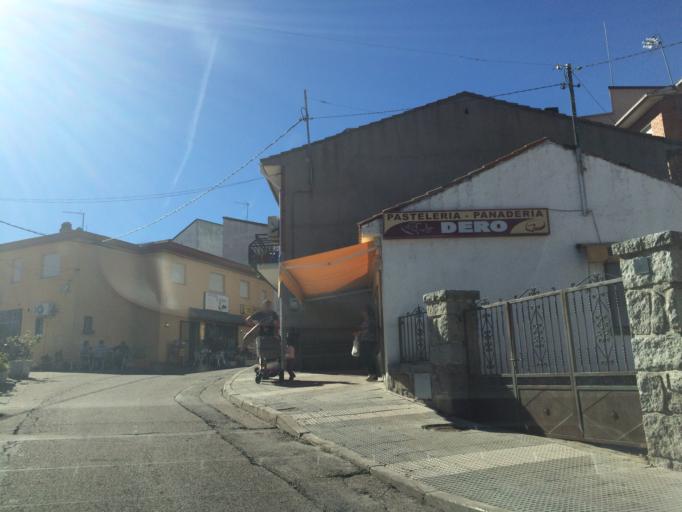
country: ES
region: Madrid
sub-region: Provincia de Madrid
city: Boalo
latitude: 40.7176
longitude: -3.9196
